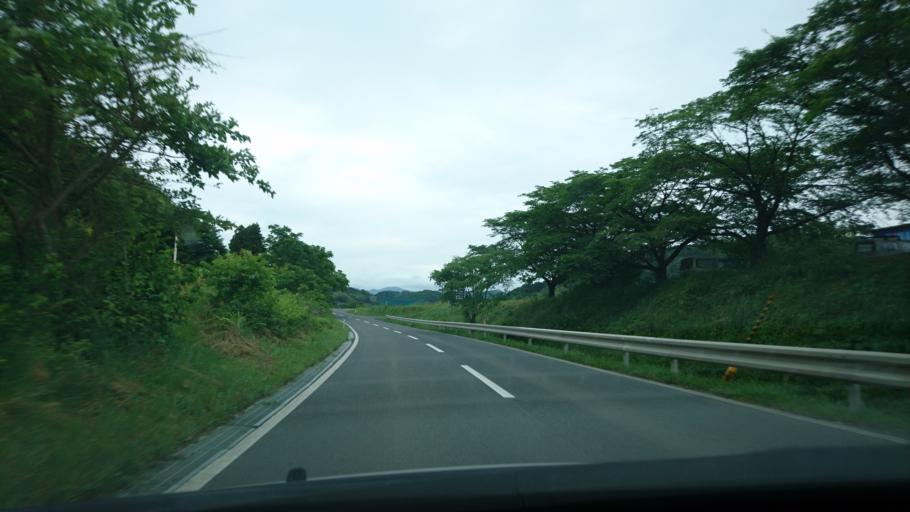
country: JP
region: Iwate
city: Ichinoseki
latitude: 38.9687
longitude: 141.2404
